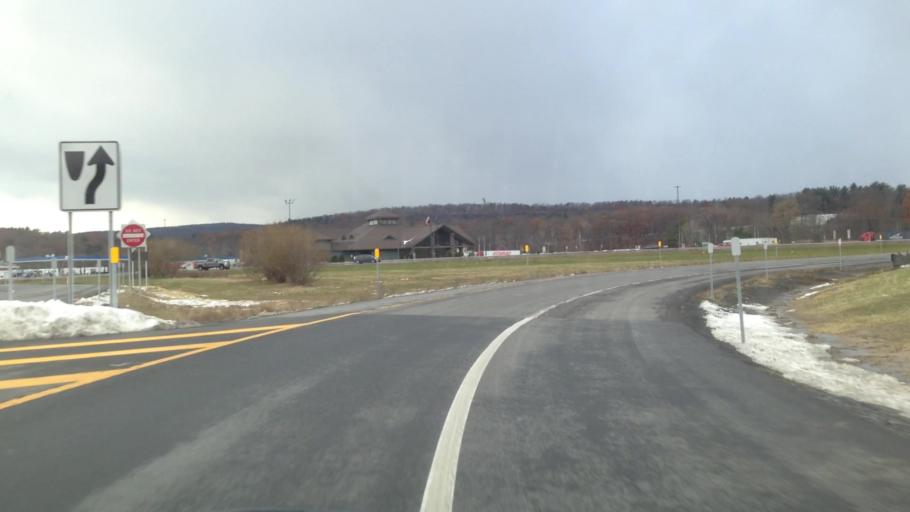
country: US
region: New York
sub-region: Albany County
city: Ravena
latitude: 42.4279
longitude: -73.8025
